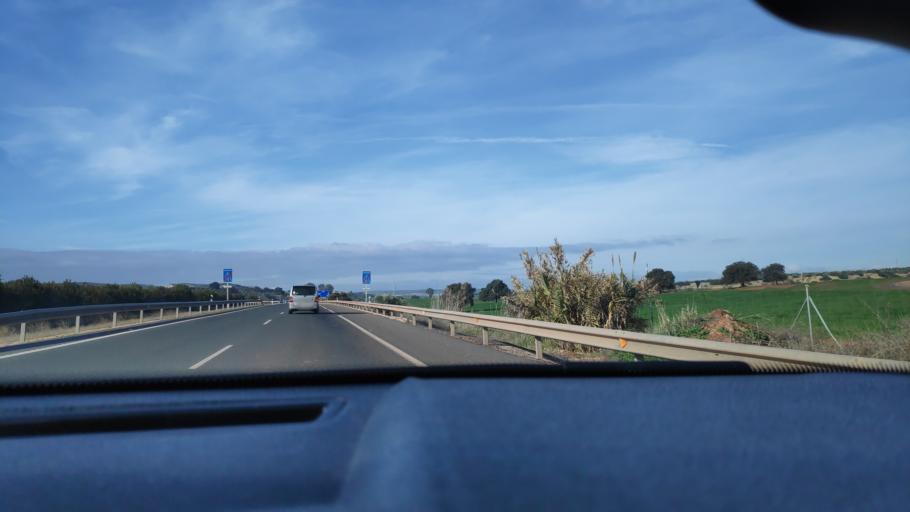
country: ES
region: Andalusia
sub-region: Provincia de Jaen
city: Bailen
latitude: 38.0977
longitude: -3.7248
